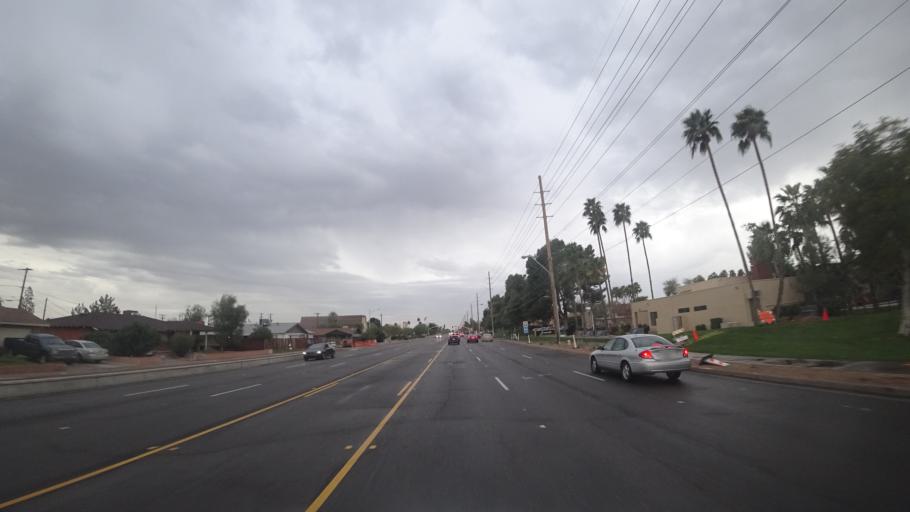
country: US
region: Arizona
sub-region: Maricopa County
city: Scottsdale
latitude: 33.4899
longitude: -111.9089
